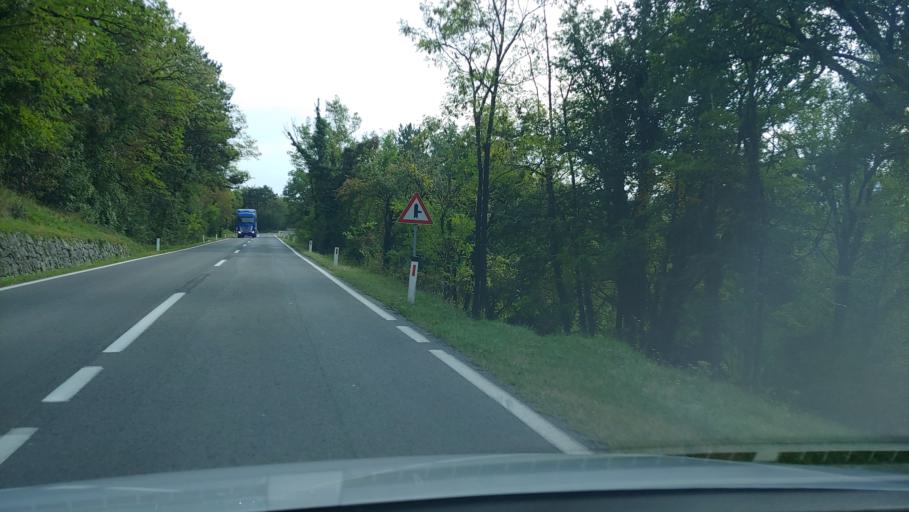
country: SI
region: Nova Gorica
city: Sempas
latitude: 45.9023
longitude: 13.7802
